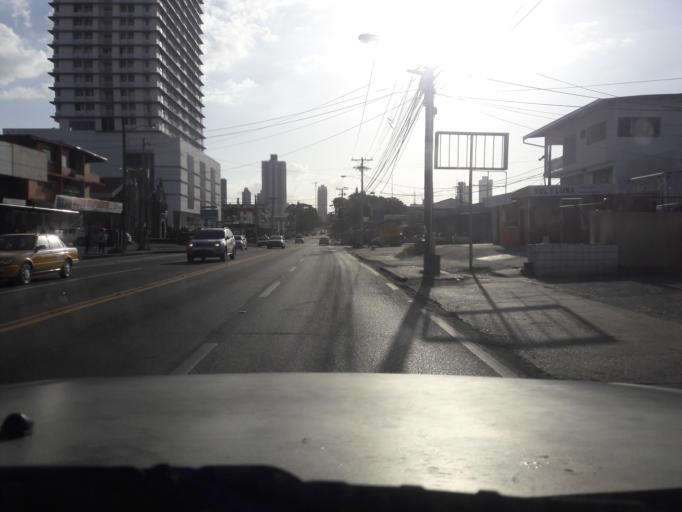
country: PA
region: Panama
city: Panama
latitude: 9.0151
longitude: -79.4985
